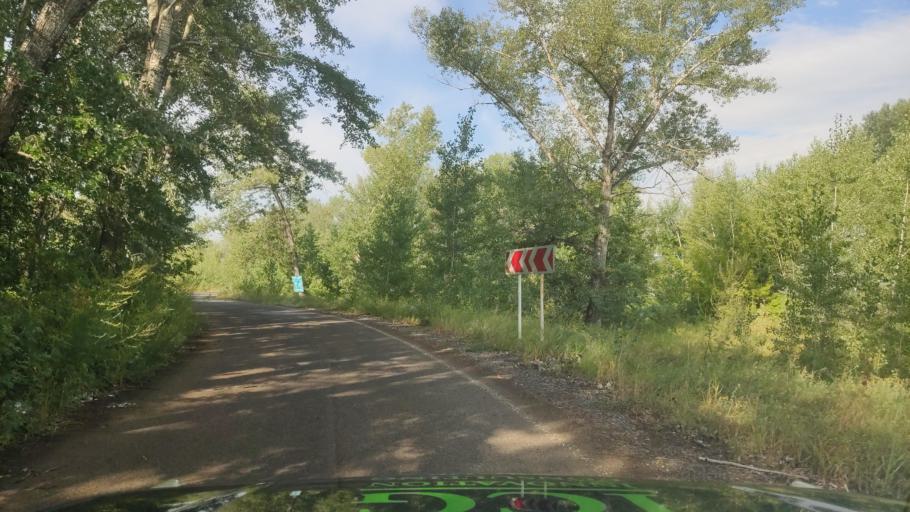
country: KZ
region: Pavlodar
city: Leninskiy
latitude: 52.4769
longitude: 76.8026
